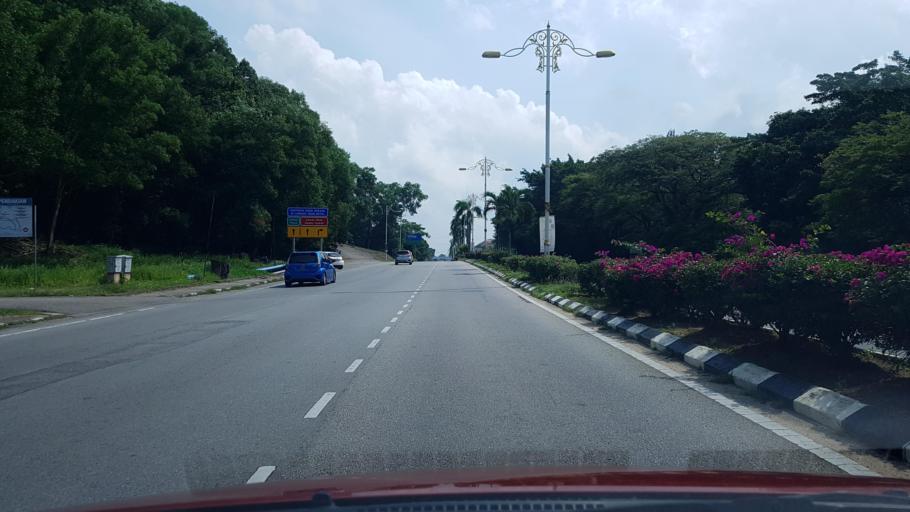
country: MY
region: Terengganu
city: Kuala Terengganu
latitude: 5.3115
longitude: 103.1339
